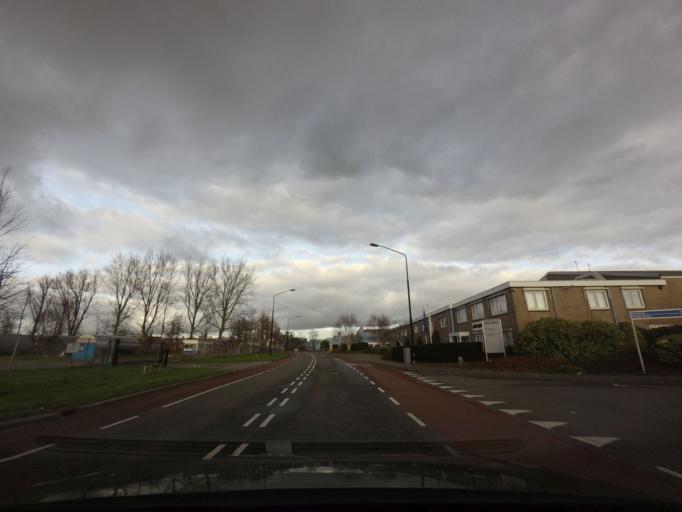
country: NL
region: North Holland
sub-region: Gemeente Heerhugowaard
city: Heerhugowaard
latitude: 52.6799
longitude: 4.8338
